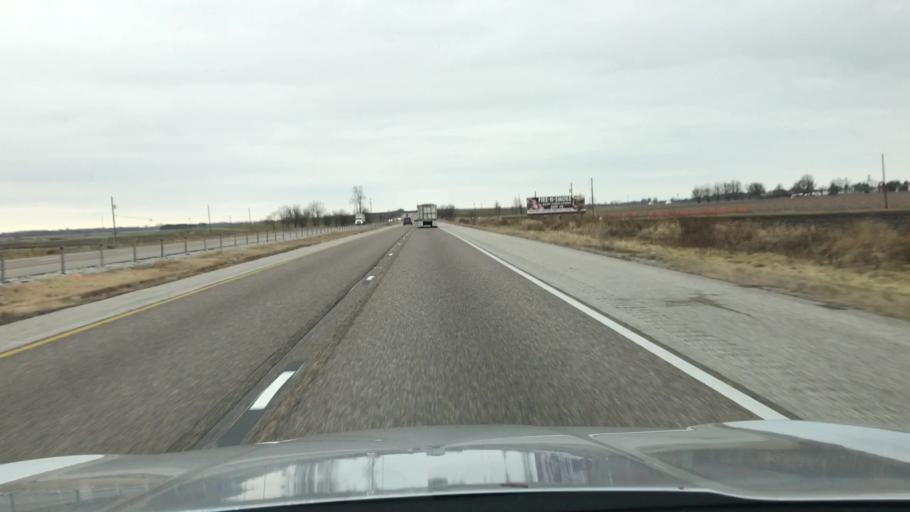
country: US
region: Illinois
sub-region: Madison County
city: Edwardsville
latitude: 38.8361
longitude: -89.8755
